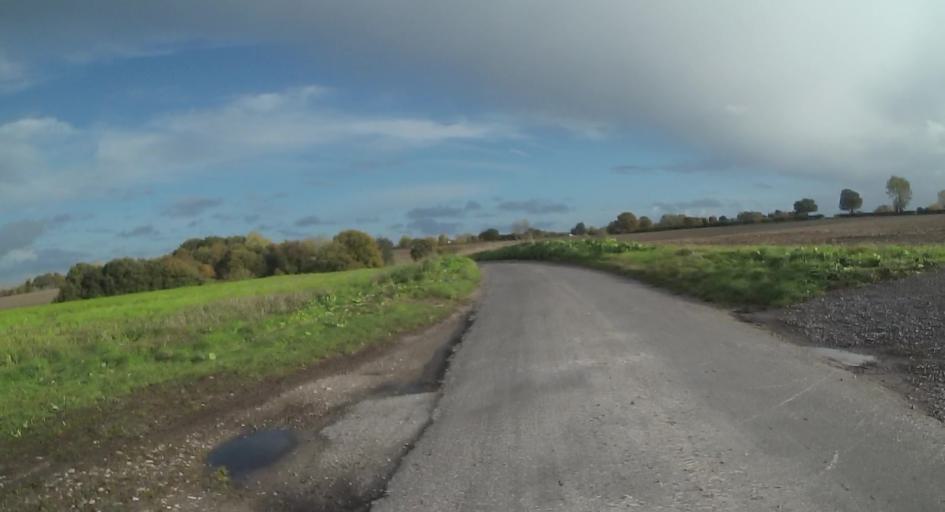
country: GB
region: England
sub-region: Hampshire
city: Kingsley
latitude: 51.1699
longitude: -0.9109
